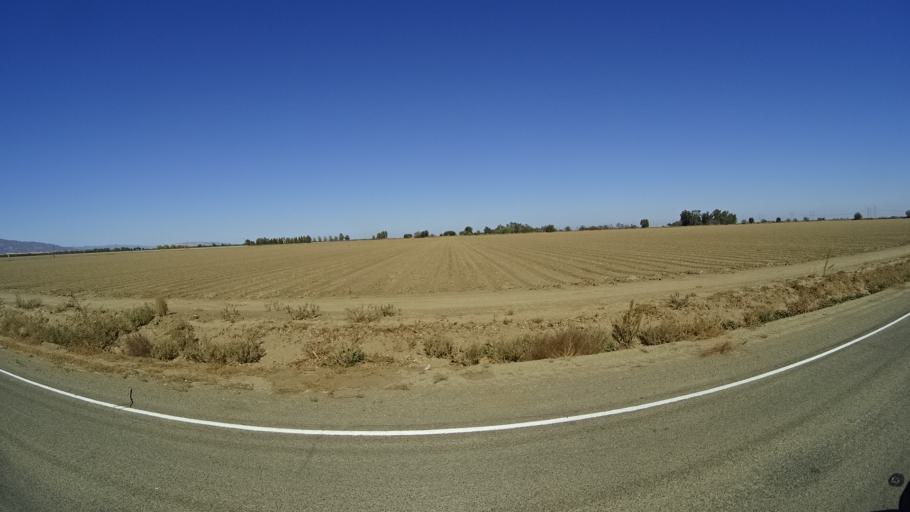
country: US
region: California
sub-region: Yolo County
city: Winters
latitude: 38.5618
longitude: -121.9404
